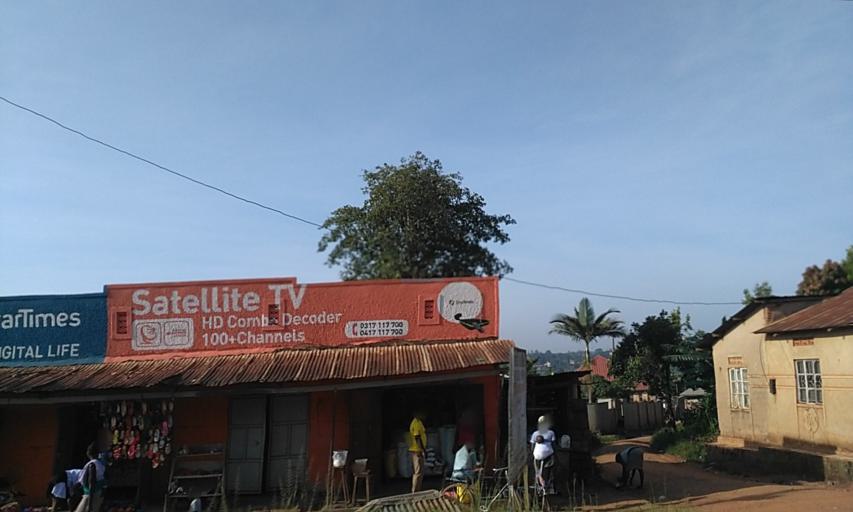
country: UG
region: Central Region
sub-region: Wakiso District
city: Bweyogerere
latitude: 0.4603
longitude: 32.6288
